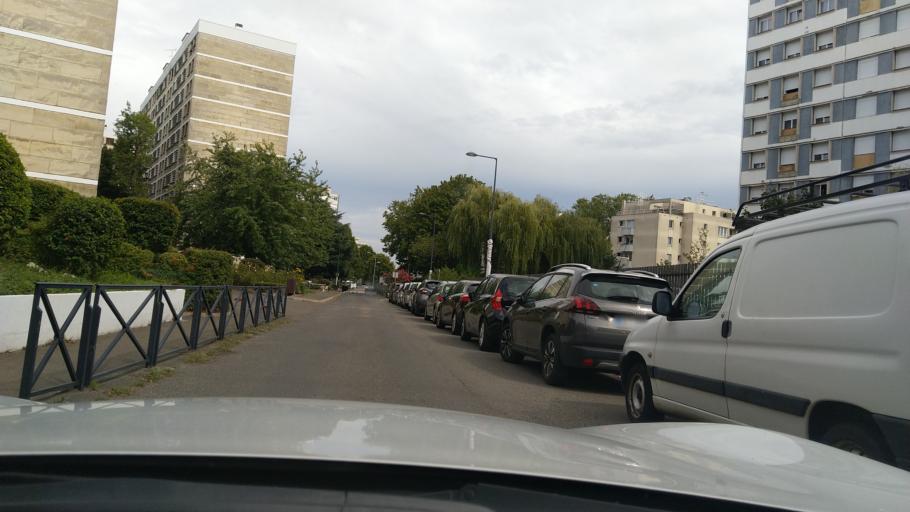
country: FR
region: Ile-de-France
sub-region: Departement de l'Essonne
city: Bievres
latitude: 48.7848
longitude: 2.2296
